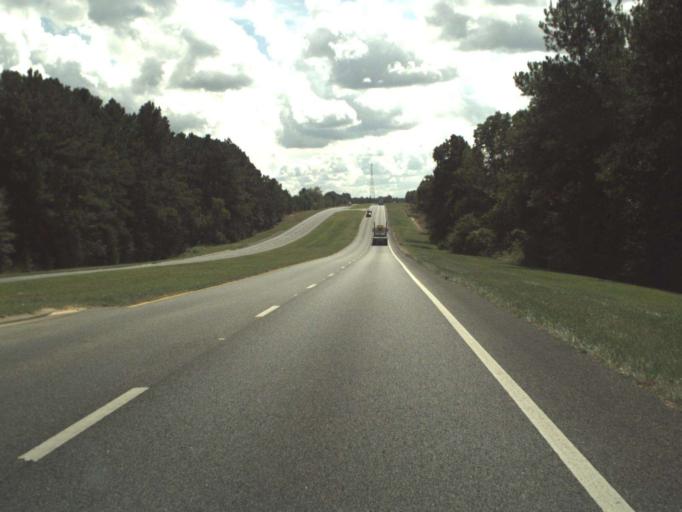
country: US
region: Florida
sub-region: Bay County
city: Youngstown
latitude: 30.5523
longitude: -85.3905
